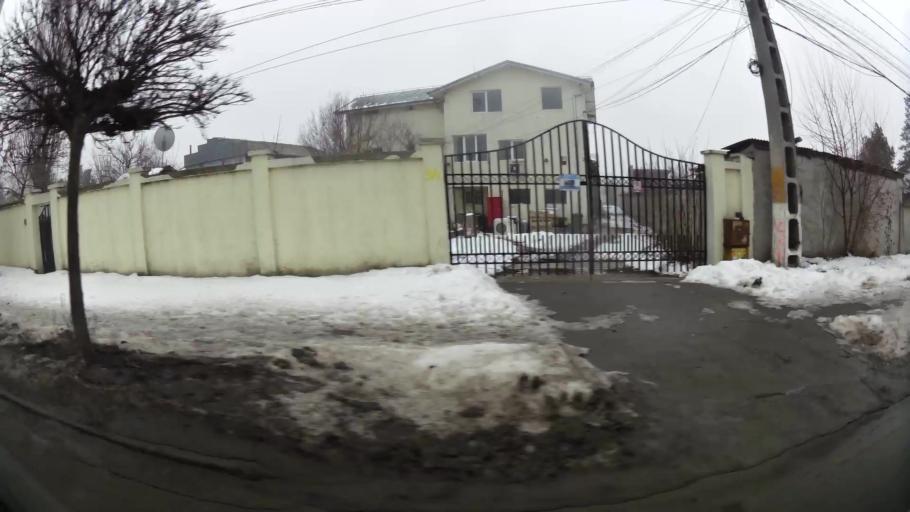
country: RO
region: Ilfov
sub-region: Comuna Chiajna
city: Chiajna
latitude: 44.4541
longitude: 25.9903
